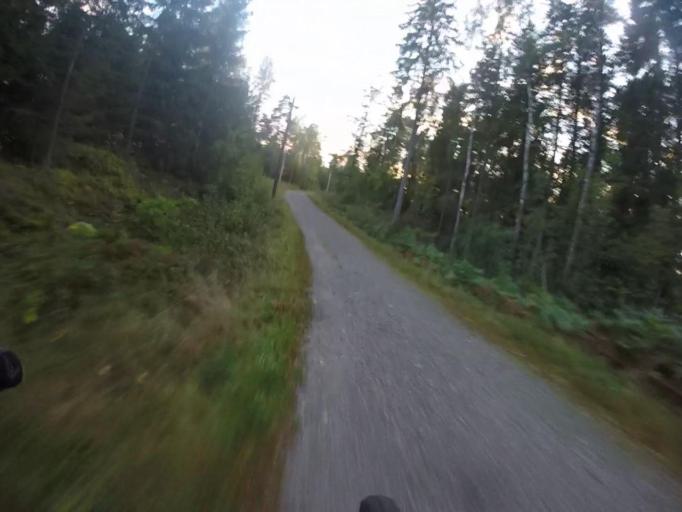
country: SE
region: Vaestra Goetaland
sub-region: Trollhattan
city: Trollhattan
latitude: 58.3038
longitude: 12.2671
